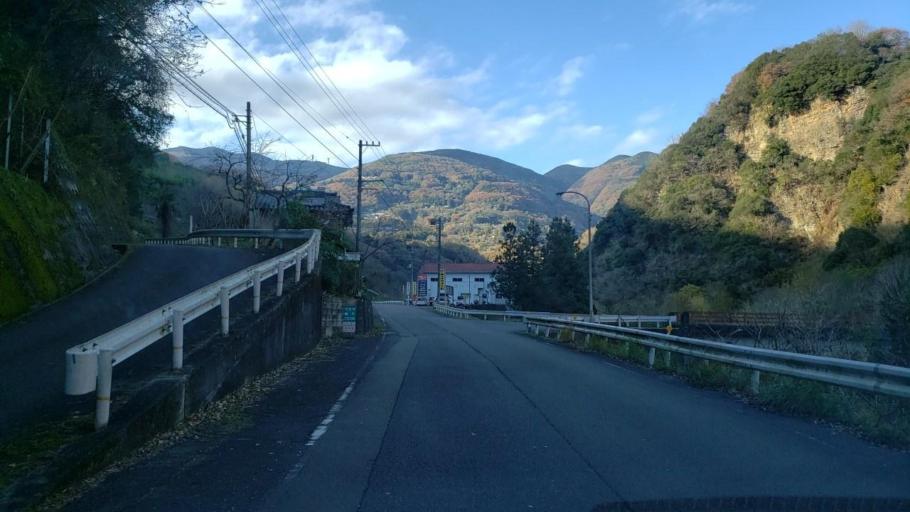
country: JP
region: Tokushima
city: Wakimachi
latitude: 34.0856
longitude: 134.0731
